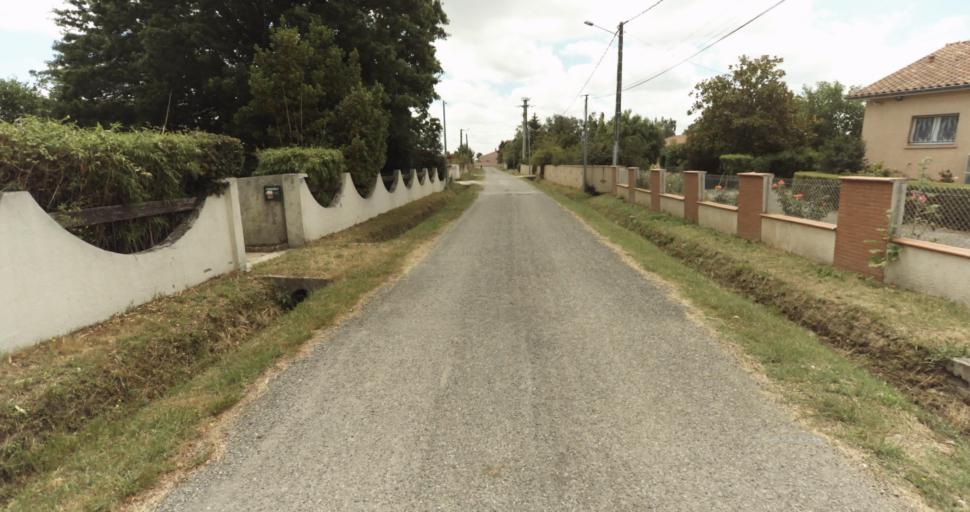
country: FR
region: Midi-Pyrenees
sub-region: Departement de la Haute-Garonne
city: Fontenilles
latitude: 43.5454
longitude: 1.1812
